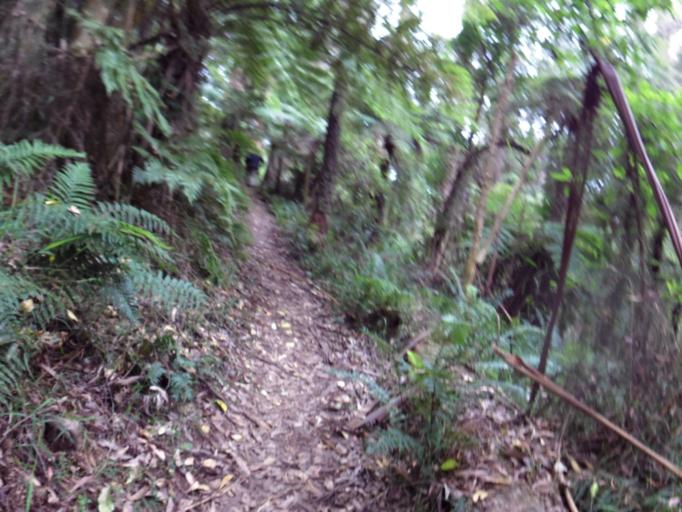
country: AU
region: Victoria
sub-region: Yarra Ranges
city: Kallista
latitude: -37.8846
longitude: 145.3639
